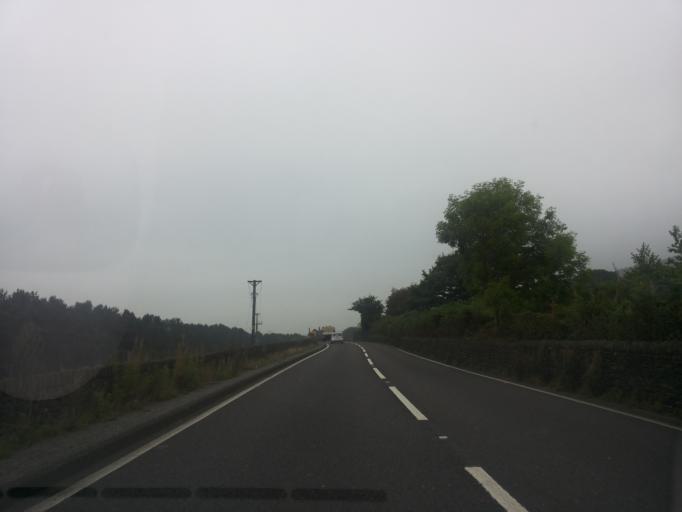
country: GB
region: England
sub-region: Derbyshire
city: Glossop
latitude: 53.4846
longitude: -1.9113
